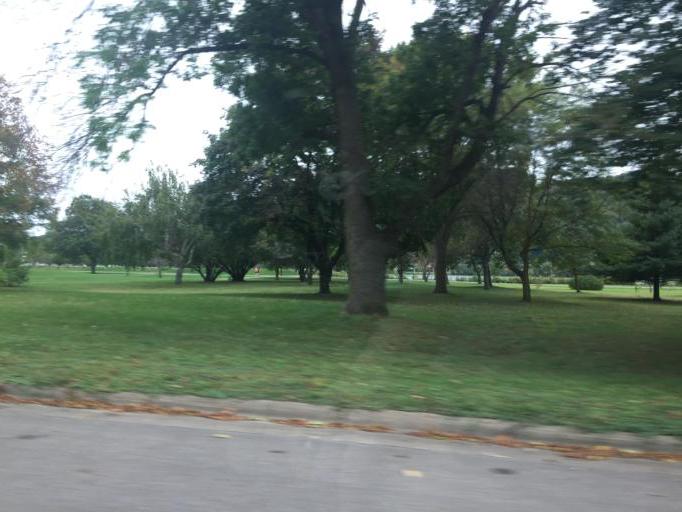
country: US
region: Minnesota
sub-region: Winona County
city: Winona
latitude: 44.0387
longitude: -91.6274
